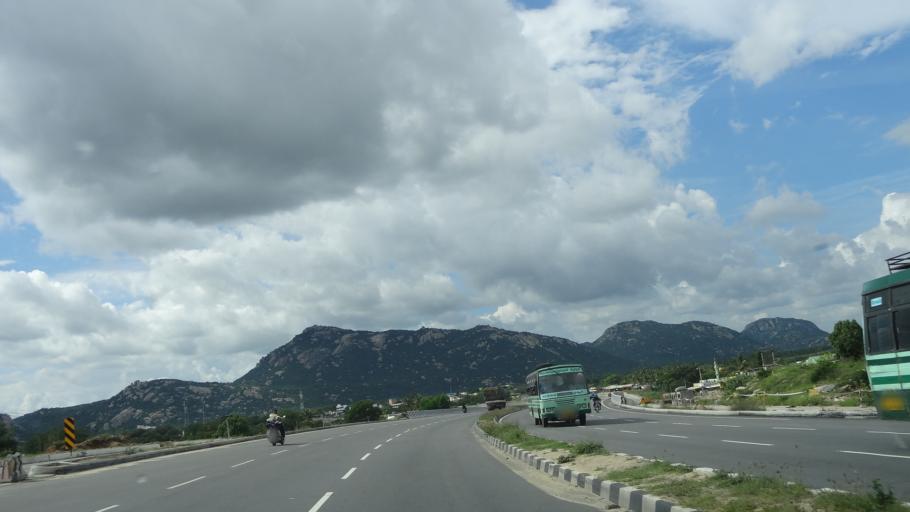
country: IN
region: Tamil Nadu
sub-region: Krishnagiri
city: Krishnagiri
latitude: 12.5928
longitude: 78.1387
